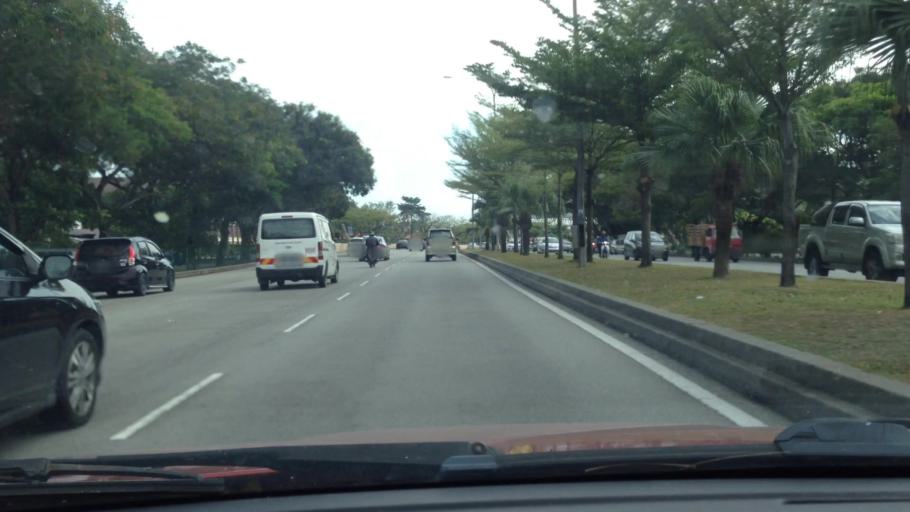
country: MY
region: Selangor
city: Subang Jaya
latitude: 3.0532
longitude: 101.5765
